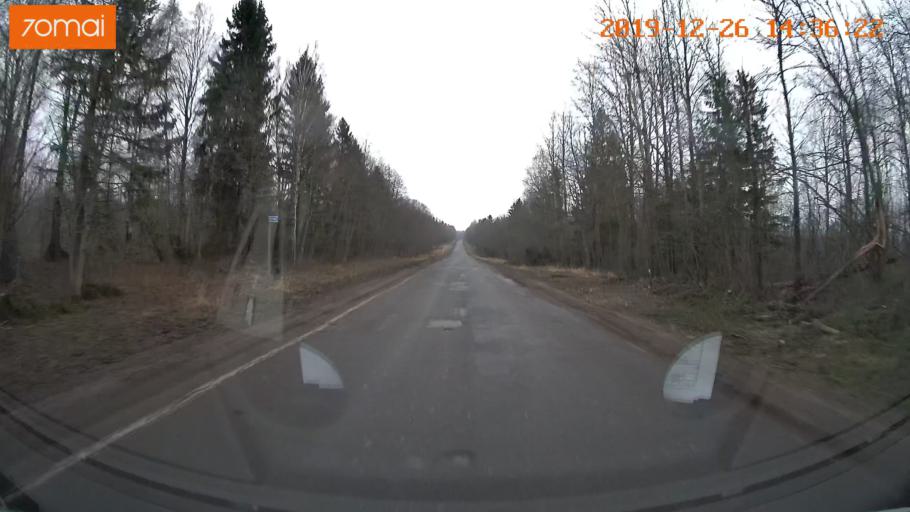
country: RU
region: Jaroslavl
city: Poshekhon'ye
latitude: 58.4120
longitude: 38.9764
